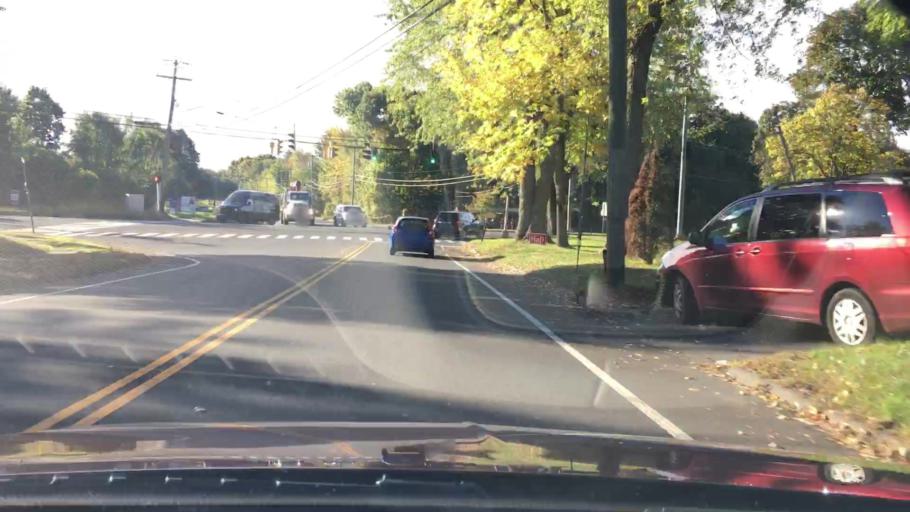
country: US
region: Connecticut
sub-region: Hartford County
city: Sherwood Manor
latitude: 42.0050
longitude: -72.5591
